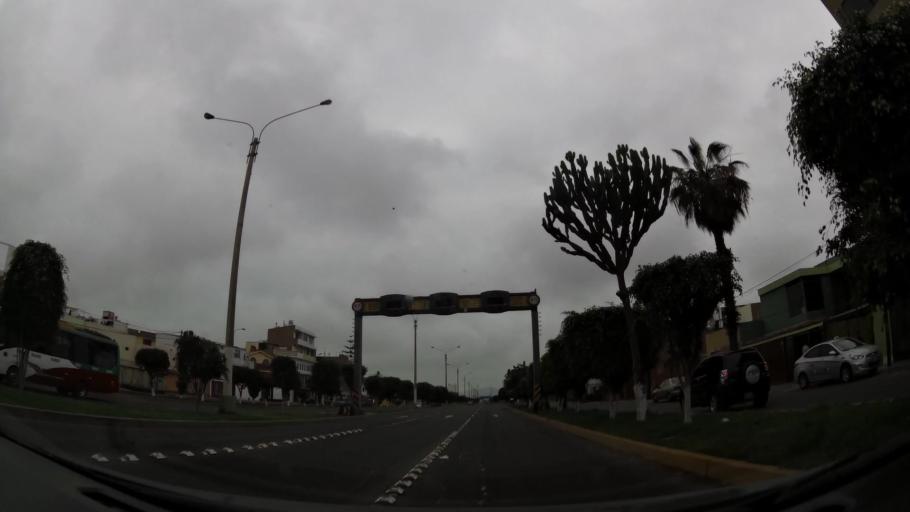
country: PE
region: Callao
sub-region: Callao
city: Callao
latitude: -12.0626
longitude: -77.0996
